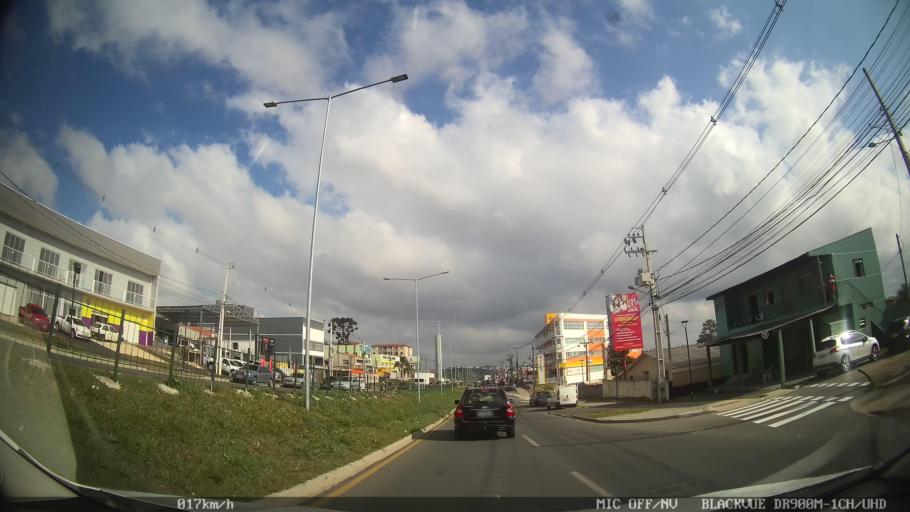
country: BR
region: Parana
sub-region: Pinhais
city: Pinhais
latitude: -25.3836
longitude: -49.1868
